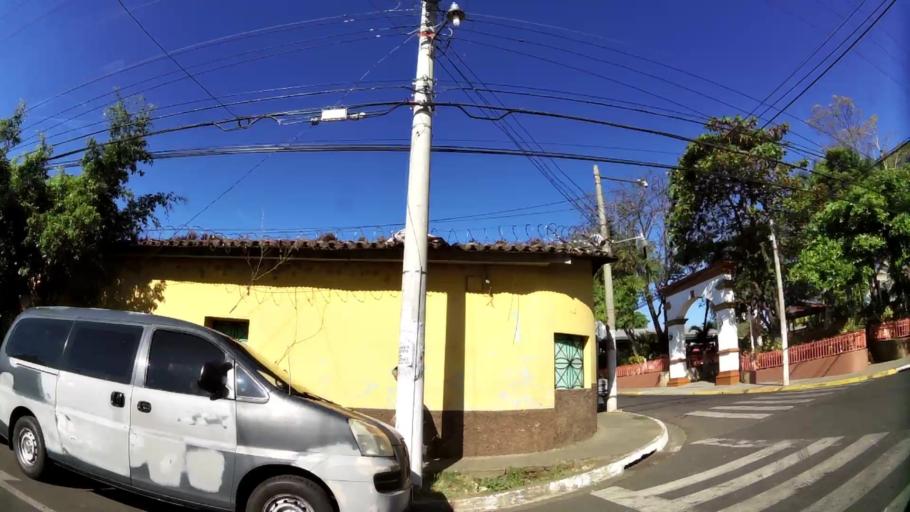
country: SV
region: Sonsonate
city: Sonzacate
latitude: 13.7354
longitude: -89.7155
